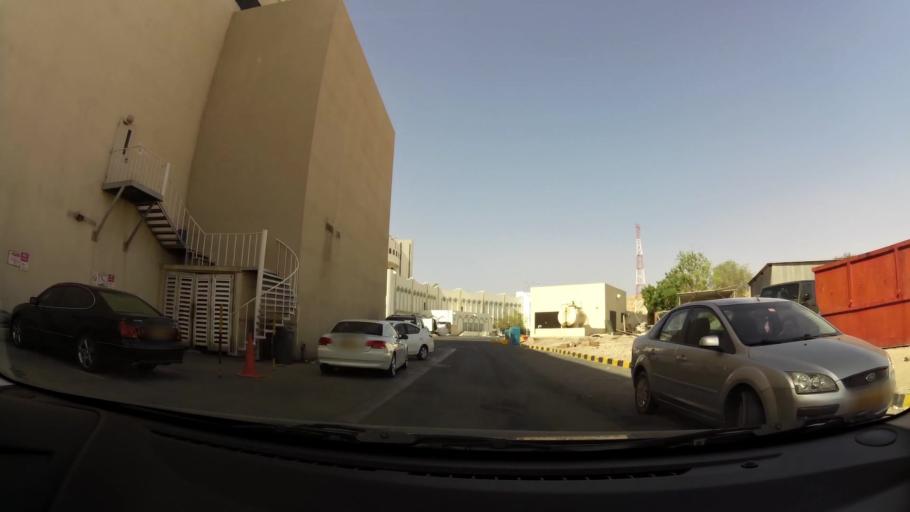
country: OM
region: Muhafazat Masqat
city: Muscat
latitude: 23.6061
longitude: 58.4993
